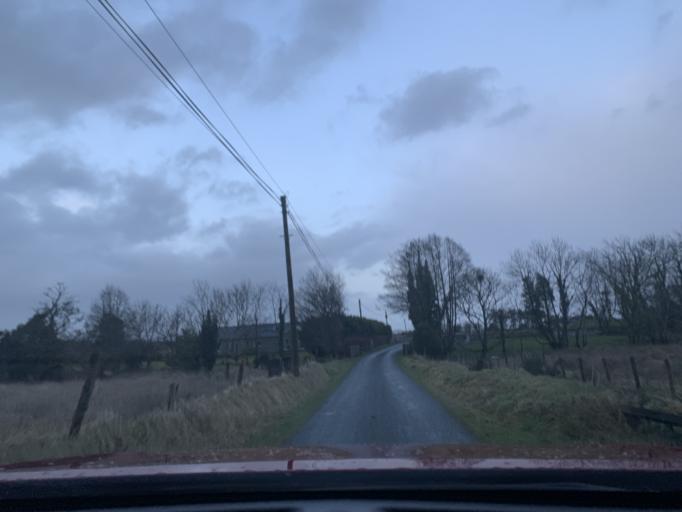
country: IE
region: Connaught
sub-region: Roscommon
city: Ballaghaderreen
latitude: 53.9796
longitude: -8.5504
